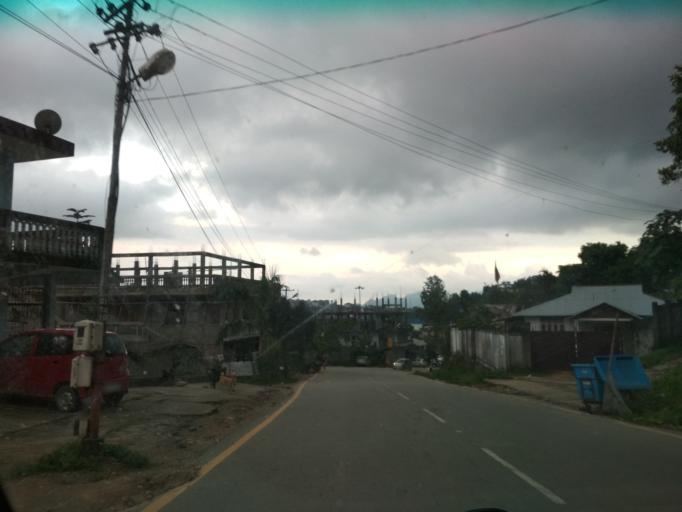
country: IN
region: Arunachal Pradesh
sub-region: Papum Pare
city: Itanagar
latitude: 27.1009
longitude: 93.6159
